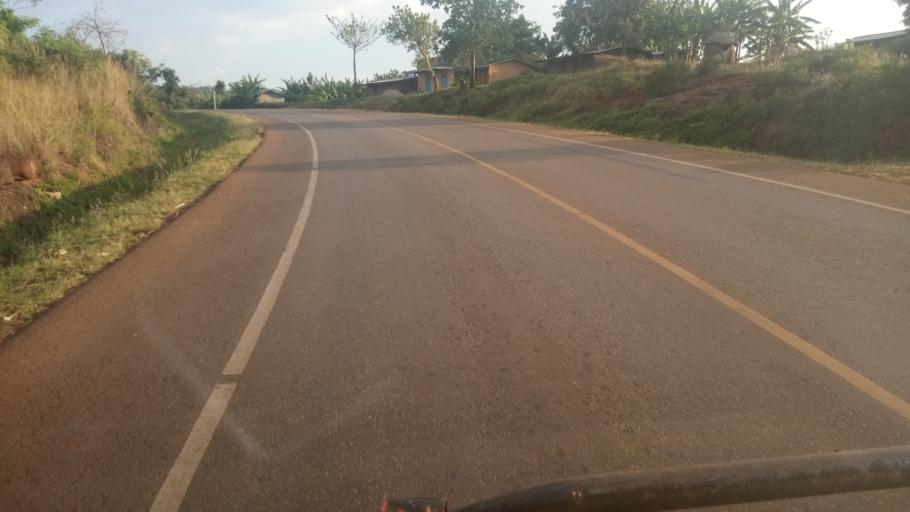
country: UG
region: Eastern Region
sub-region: Sironko District
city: Sironko
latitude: 1.3340
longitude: 34.3221
